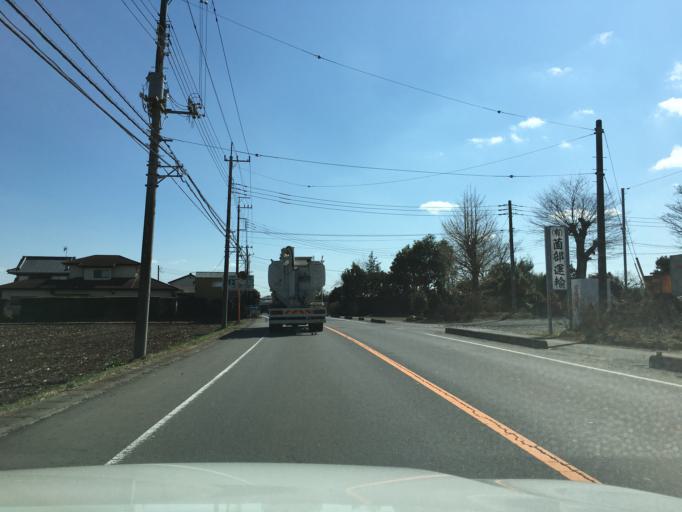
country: JP
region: Tochigi
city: Karasuyama
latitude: 36.7724
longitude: 140.1255
